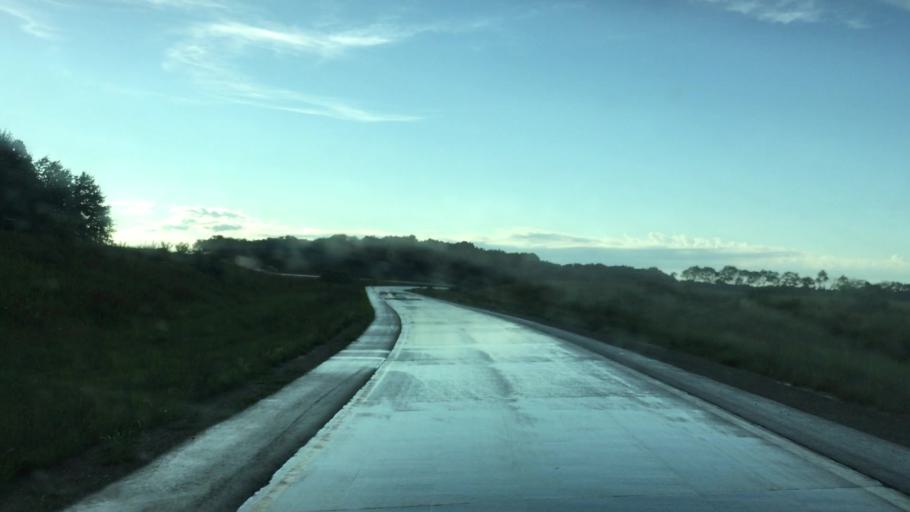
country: US
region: Iowa
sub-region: Henry County
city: Mount Pleasant
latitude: 40.9995
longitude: -91.5454
